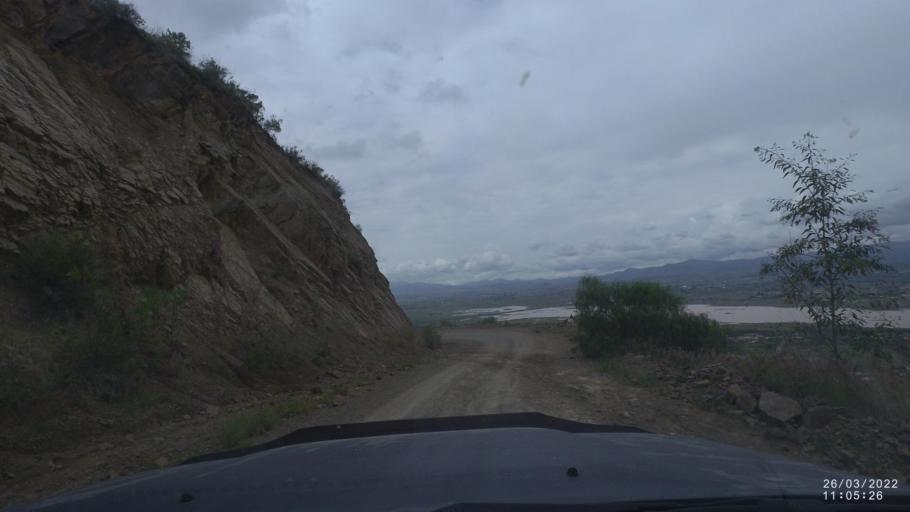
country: BO
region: Cochabamba
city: Tarata
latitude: -17.5318
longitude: -66.0228
